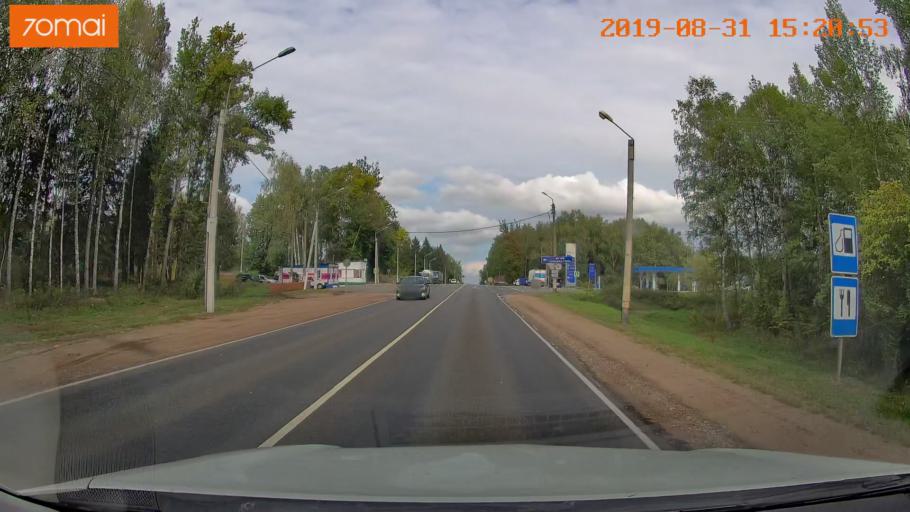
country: RU
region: Kaluga
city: Baryatino
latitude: 54.4930
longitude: 34.4442
